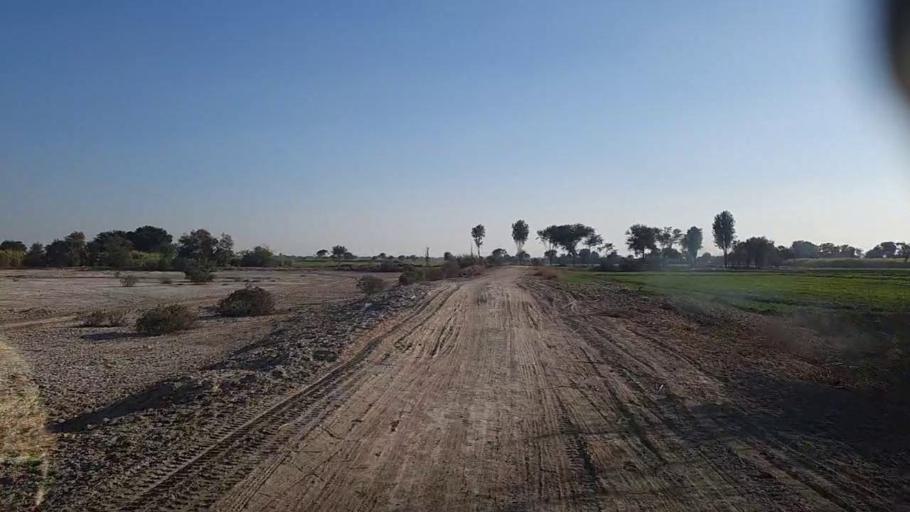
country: PK
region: Sindh
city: Khairpur
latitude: 28.0158
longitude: 69.7088
